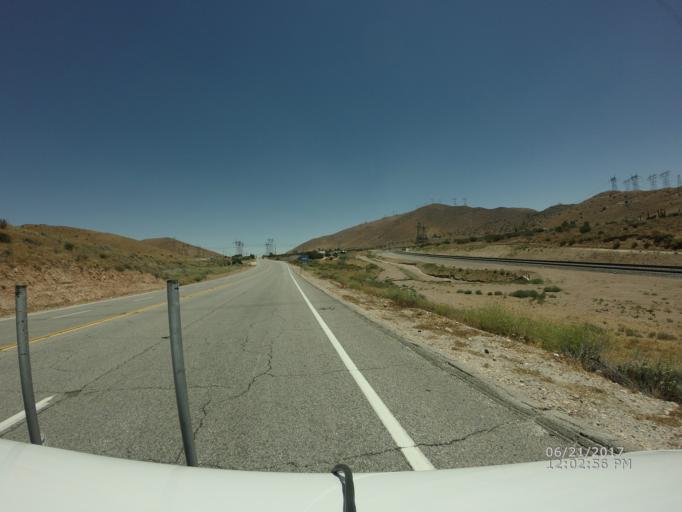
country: US
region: California
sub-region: Los Angeles County
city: Vincent
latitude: 34.4932
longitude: -118.1259
